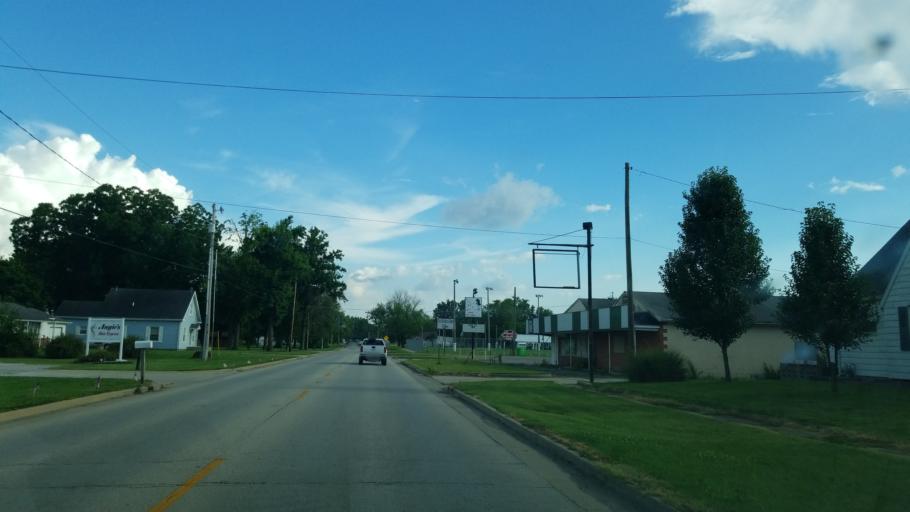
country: US
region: Illinois
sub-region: Marion County
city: Sandoval
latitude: 38.6109
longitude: -89.1151
